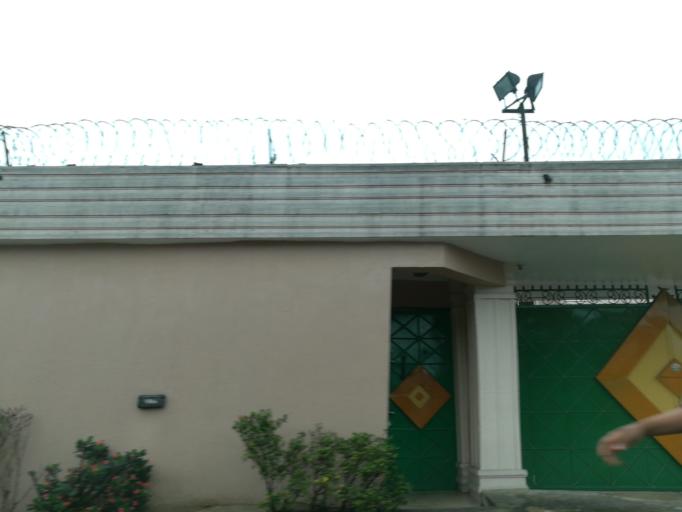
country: NG
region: Rivers
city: Port Harcourt
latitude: 4.8606
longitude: 7.0336
